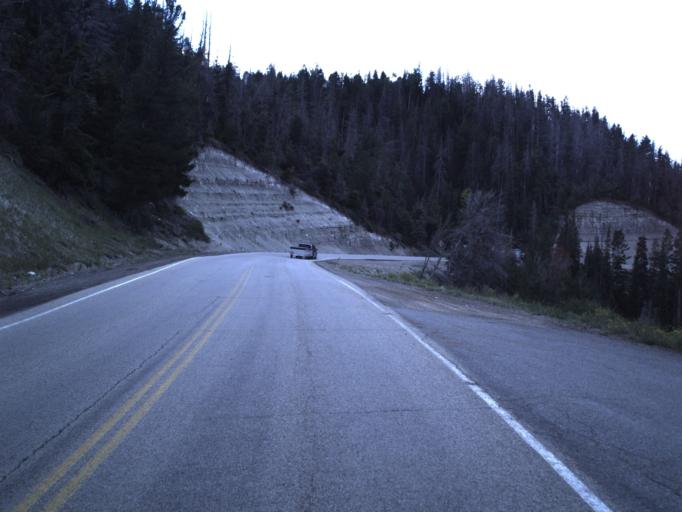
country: US
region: Utah
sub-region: Carbon County
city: Helper
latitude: 39.8924
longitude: -110.7484
